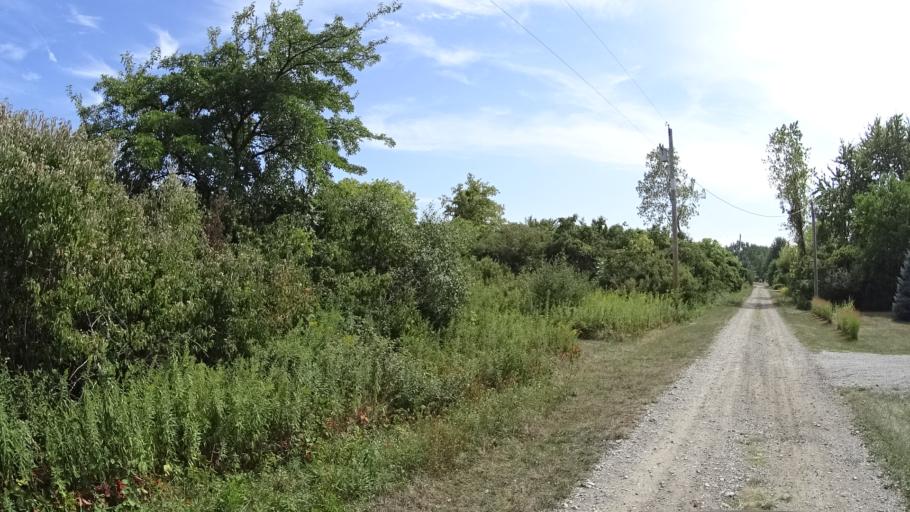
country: US
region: Ohio
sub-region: Erie County
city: Sandusky
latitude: 41.5899
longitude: -82.6933
